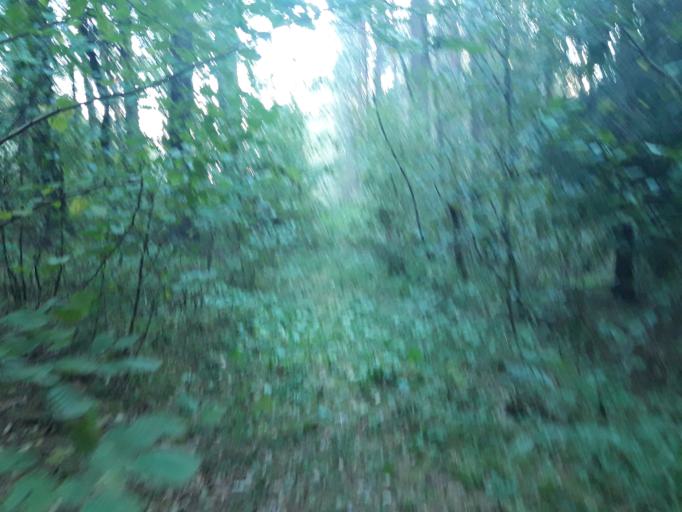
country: BY
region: Minsk
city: Pyatryshki
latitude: 54.1278
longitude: 27.1240
